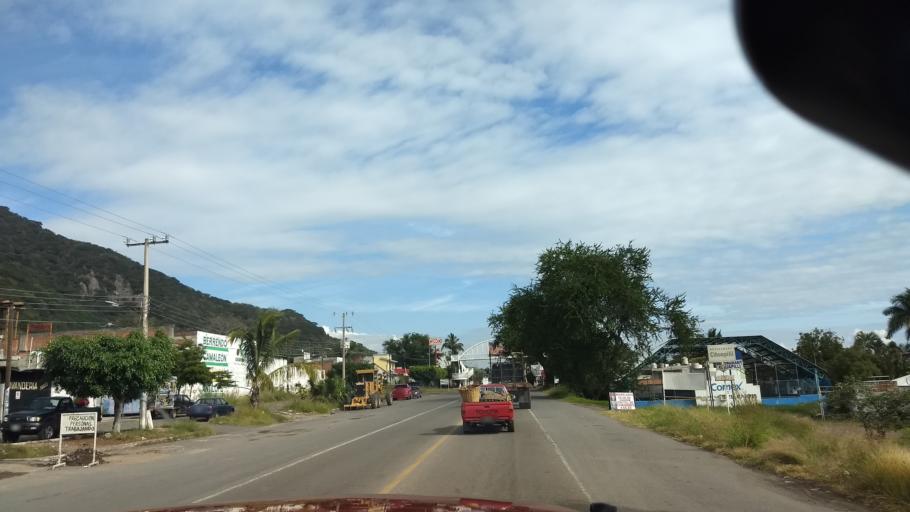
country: MX
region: Jalisco
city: Tuxpan
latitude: 19.5561
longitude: -103.3897
